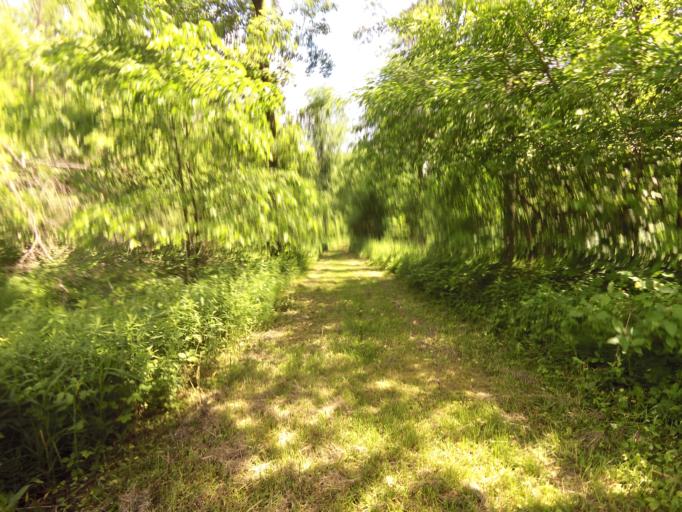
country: CA
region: Ontario
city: Ottawa
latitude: 45.3512
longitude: -75.6072
